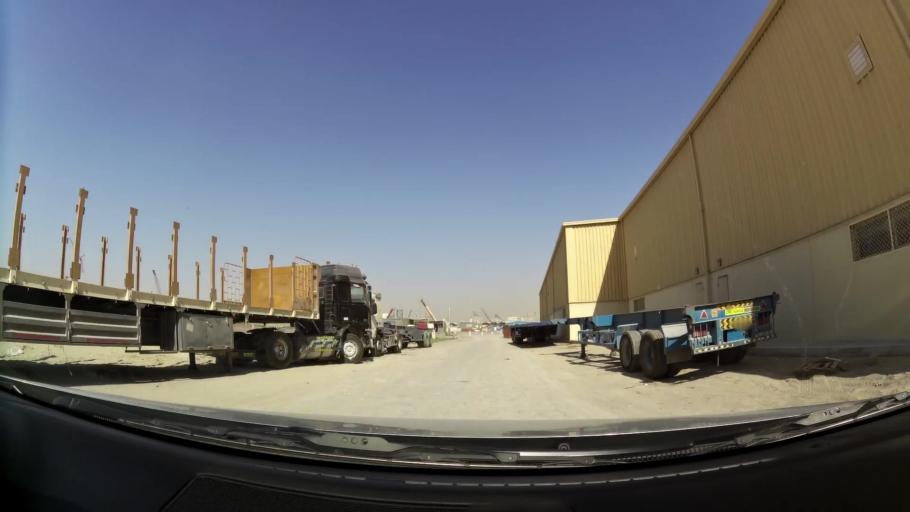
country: AE
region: Dubai
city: Dubai
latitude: 25.0042
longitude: 55.1180
